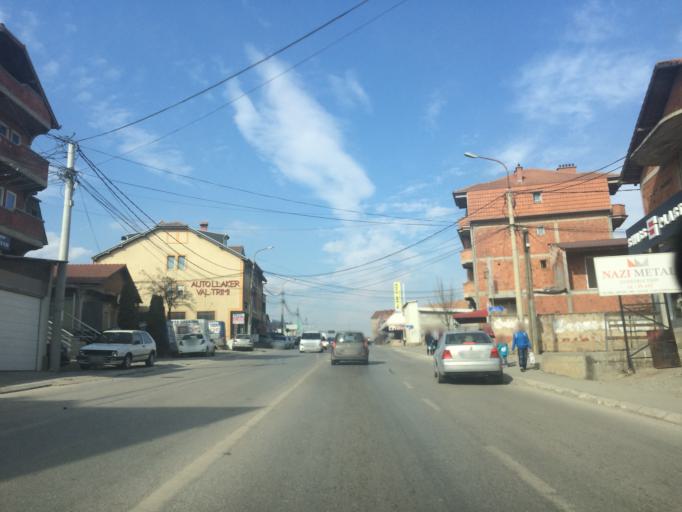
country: XK
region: Pristina
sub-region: Komuna e Prishtines
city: Pristina
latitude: 42.6849
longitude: 21.1591
